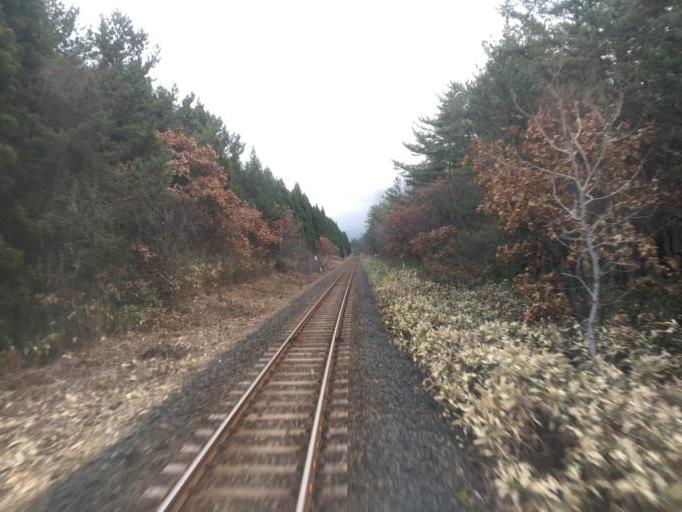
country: JP
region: Aomori
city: Mutsu
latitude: 41.0109
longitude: 141.2385
